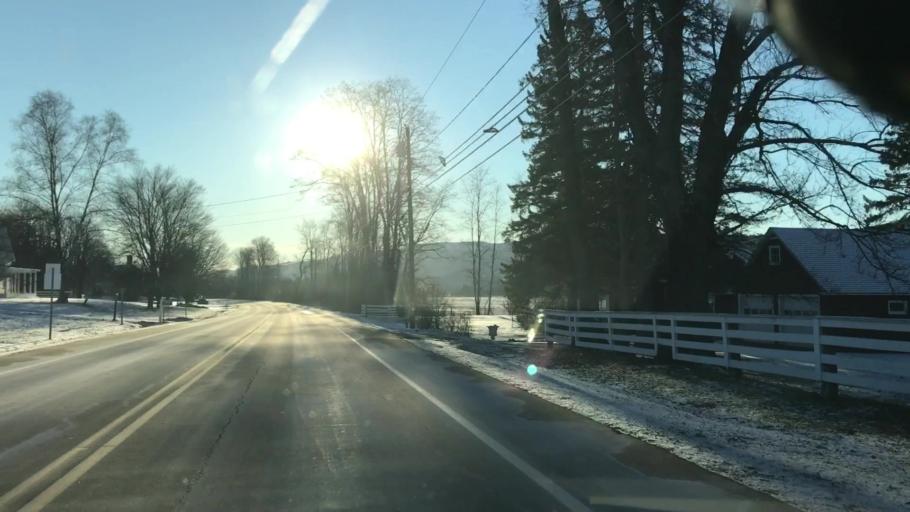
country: US
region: New Hampshire
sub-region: Grafton County
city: Orford
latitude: 43.8997
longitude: -72.1438
